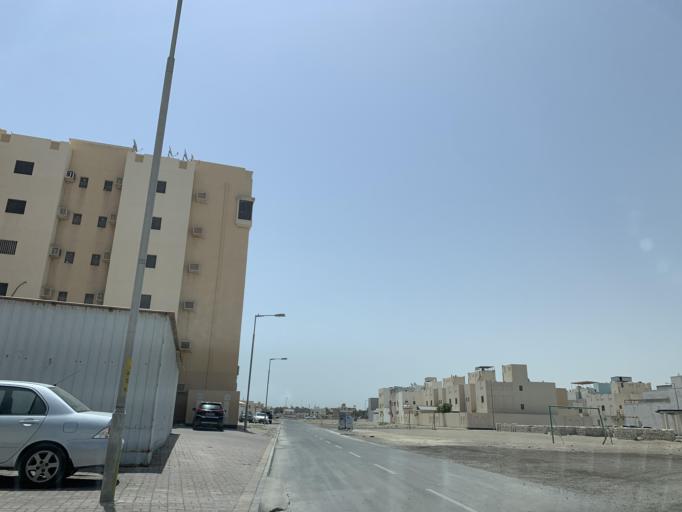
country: BH
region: Northern
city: Sitrah
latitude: 26.1420
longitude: 50.5951
